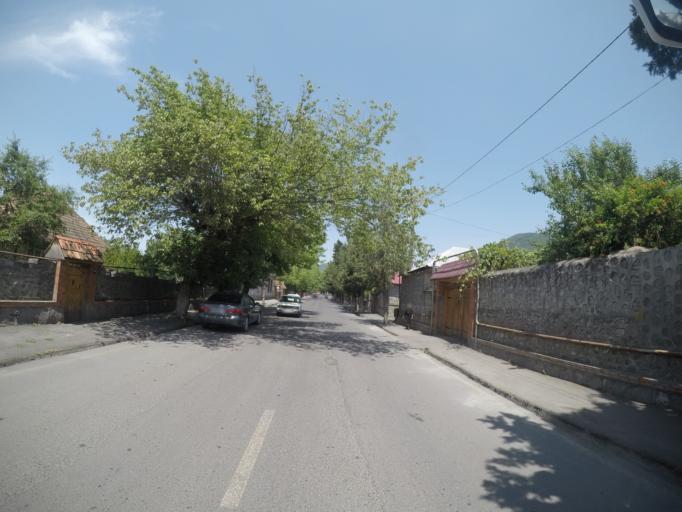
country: AZ
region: Qakh Rayon
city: Qax
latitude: 41.4175
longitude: 46.9192
